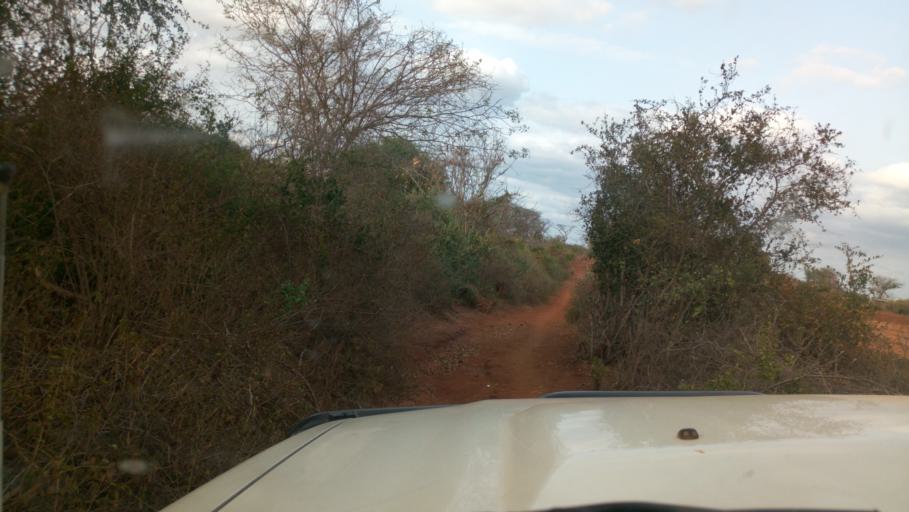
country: KE
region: Kitui
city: Kitui
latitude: -1.9760
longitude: 38.3022
